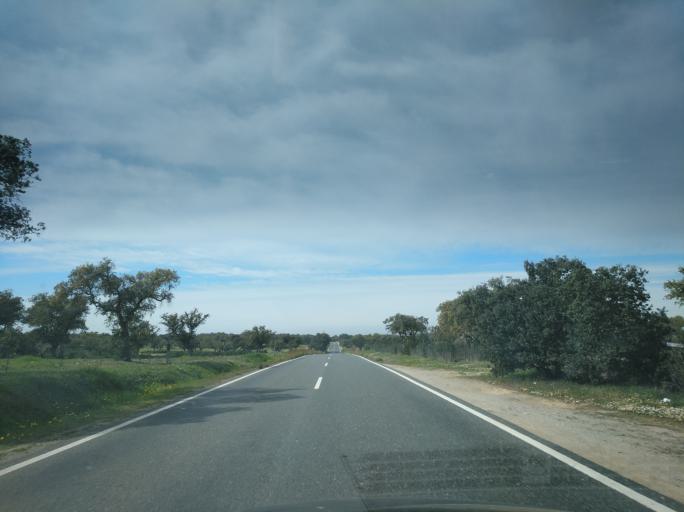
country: PT
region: Beja
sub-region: Mertola
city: Mertola
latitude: 37.7382
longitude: -7.7781
